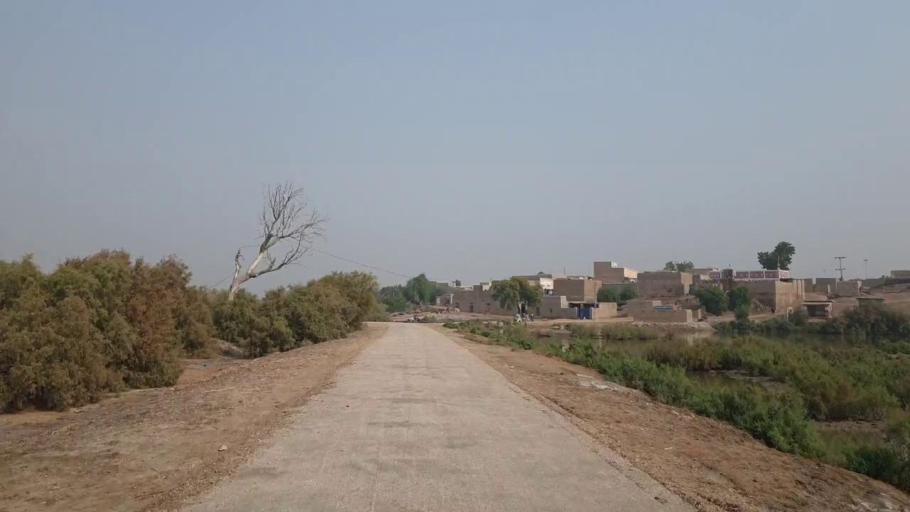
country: PK
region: Sindh
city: Bhan
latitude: 26.4889
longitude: 67.7005
